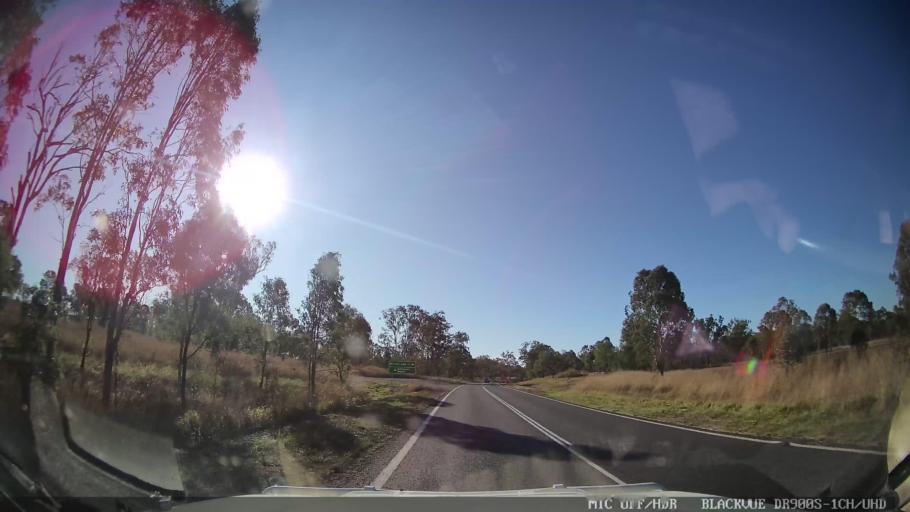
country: AU
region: Queensland
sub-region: Bundaberg
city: Sharon
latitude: -24.8245
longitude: 151.7063
